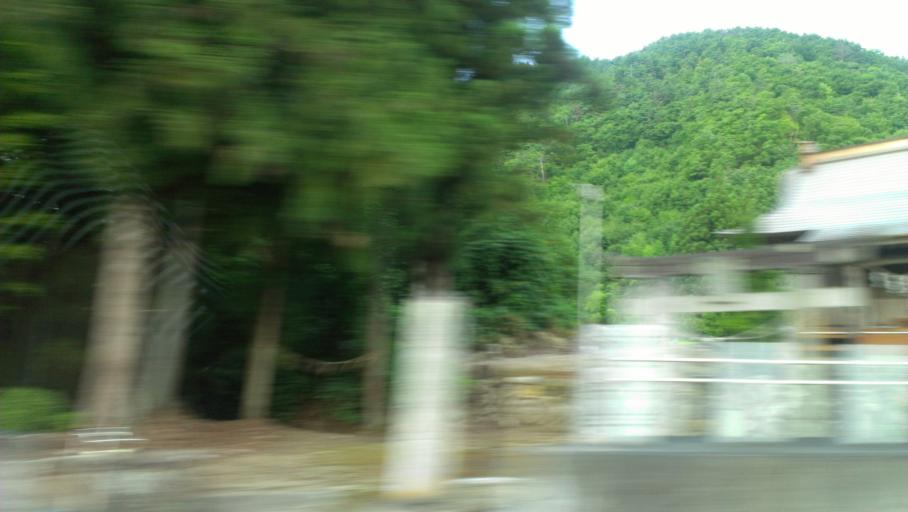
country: JP
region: Fukushima
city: Kitakata
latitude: 37.4166
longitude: 139.9028
